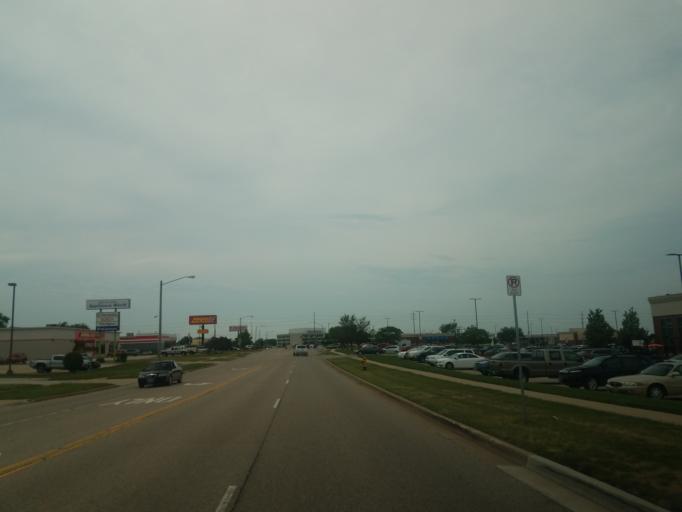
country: US
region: Illinois
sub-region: McLean County
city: Normal
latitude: 40.4967
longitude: -88.9495
